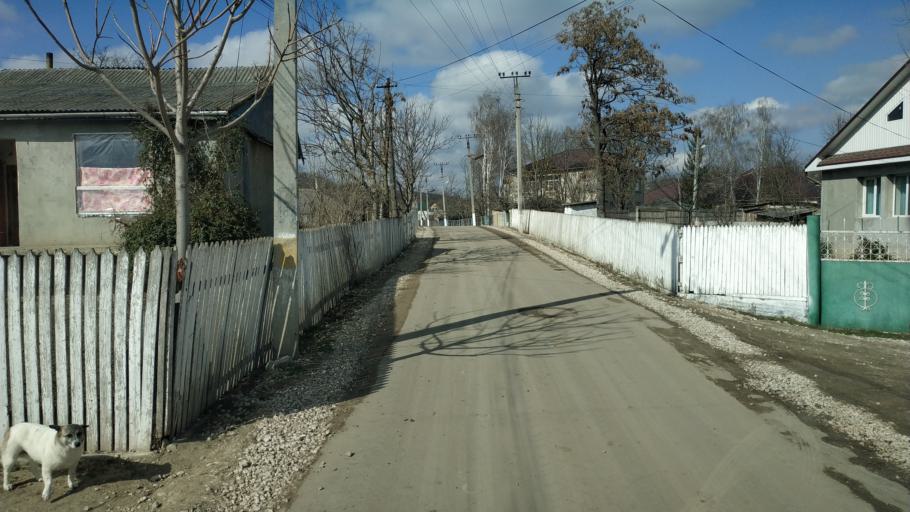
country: MD
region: Hincesti
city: Hincesti
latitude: 46.8822
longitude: 28.6186
